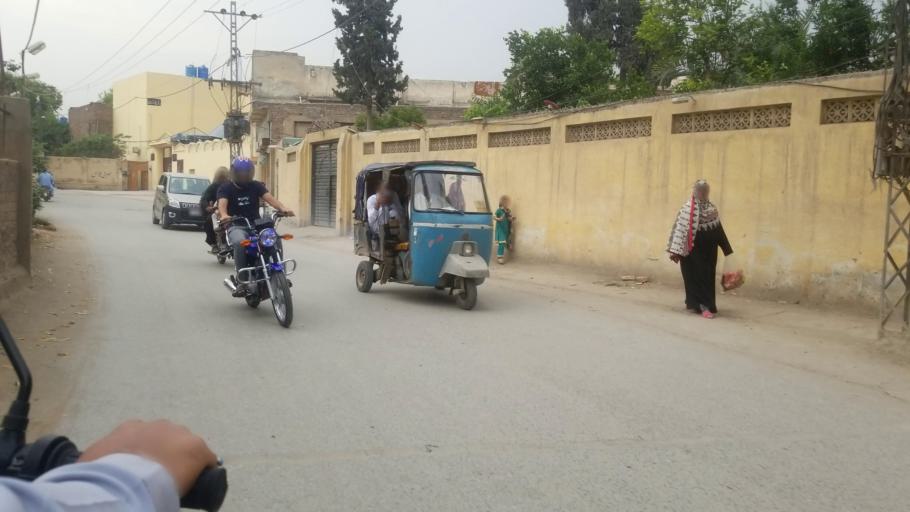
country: PK
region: Khyber Pakhtunkhwa
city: Peshawar
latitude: 33.9946
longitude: 71.5620
